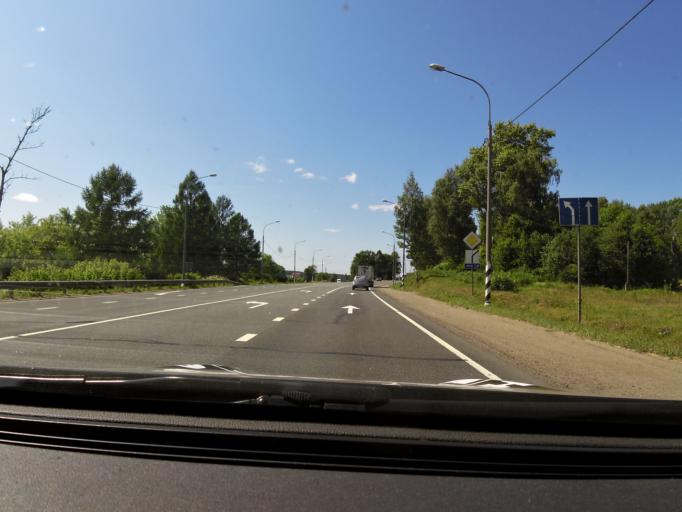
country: RU
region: Novgorod
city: Valday
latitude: 58.0306
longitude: 32.9813
